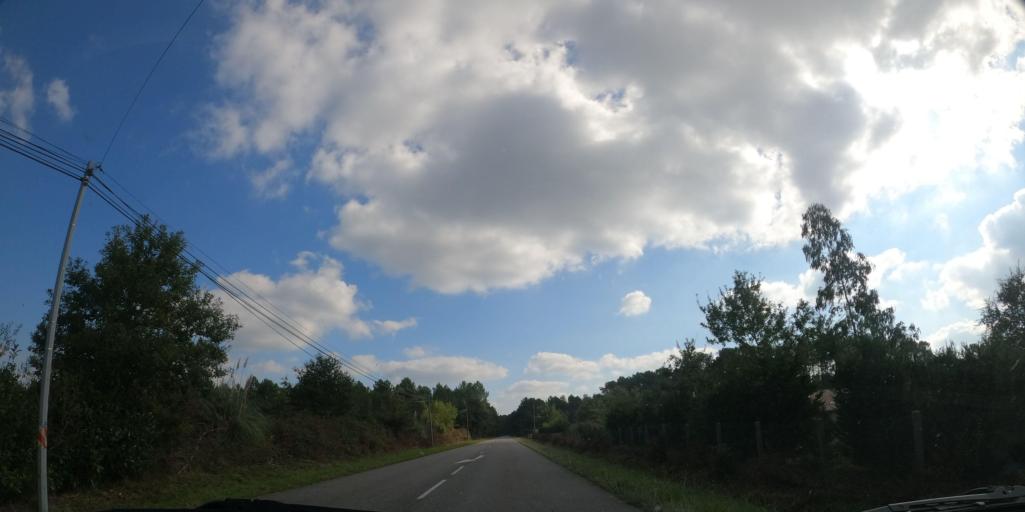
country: FR
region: Aquitaine
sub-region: Departement des Landes
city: Soustons
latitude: 43.7409
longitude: -1.2982
